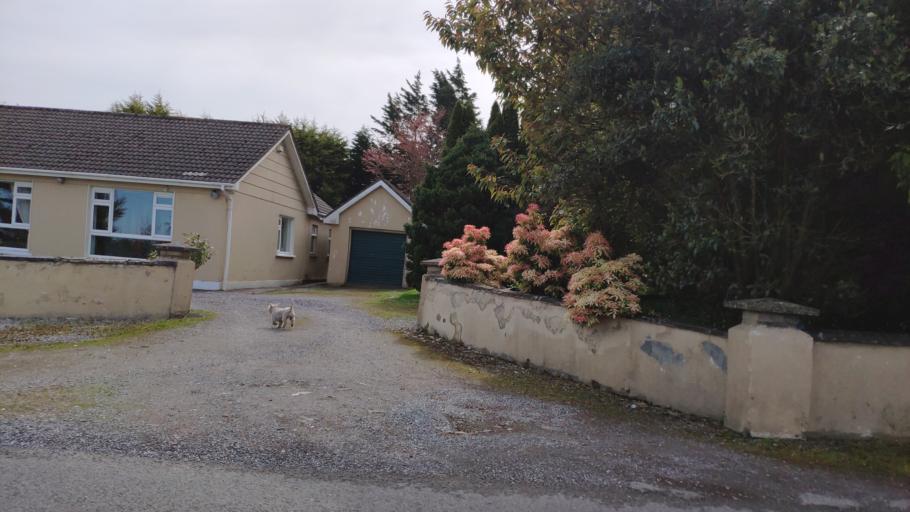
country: IE
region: Munster
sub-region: County Cork
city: Blarney
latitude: 51.9844
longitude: -8.5124
